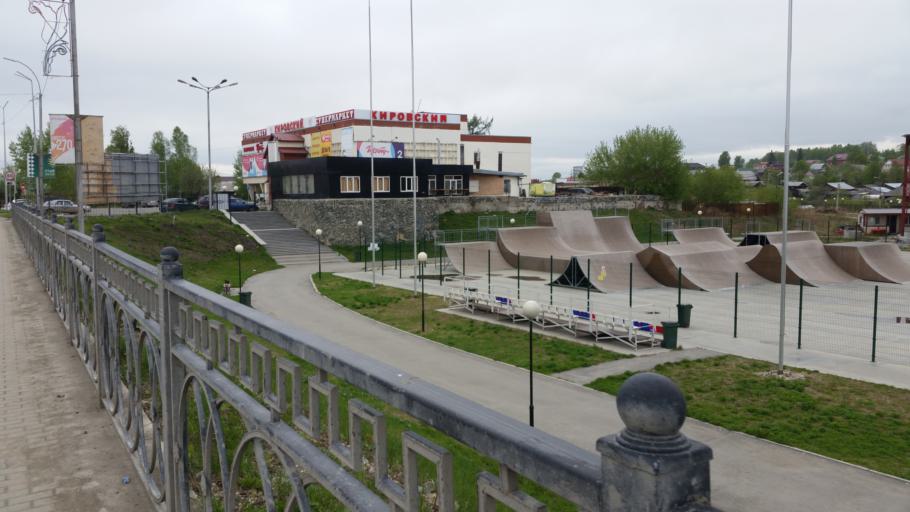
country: RU
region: Sverdlovsk
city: Beryozovsky
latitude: 56.9110
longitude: 60.7981
